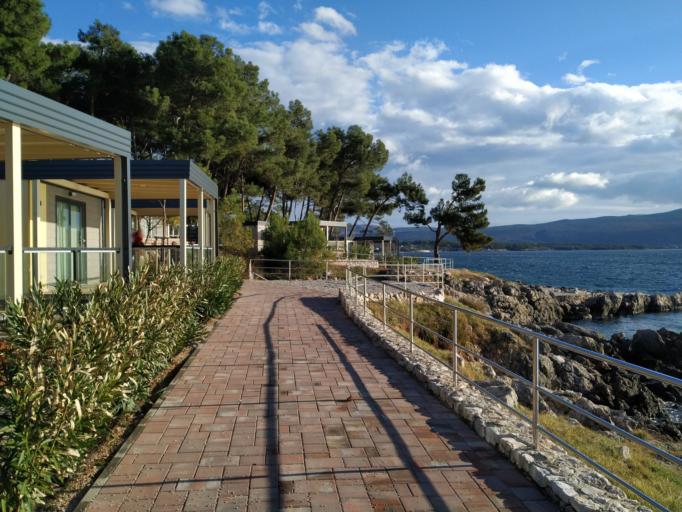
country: HR
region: Primorsko-Goranska
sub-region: Grad Krk
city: Krk
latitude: 45.0179
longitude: 14.5683
